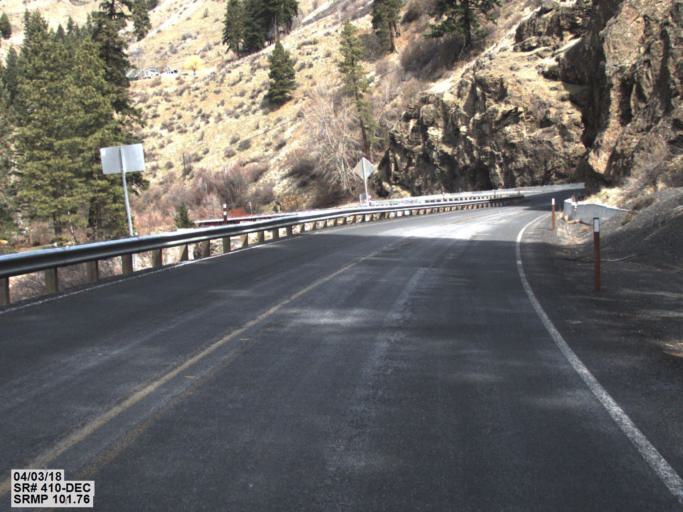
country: US
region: Washington
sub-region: Yakima County
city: Tieton
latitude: 46.8868
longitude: -120.9874
